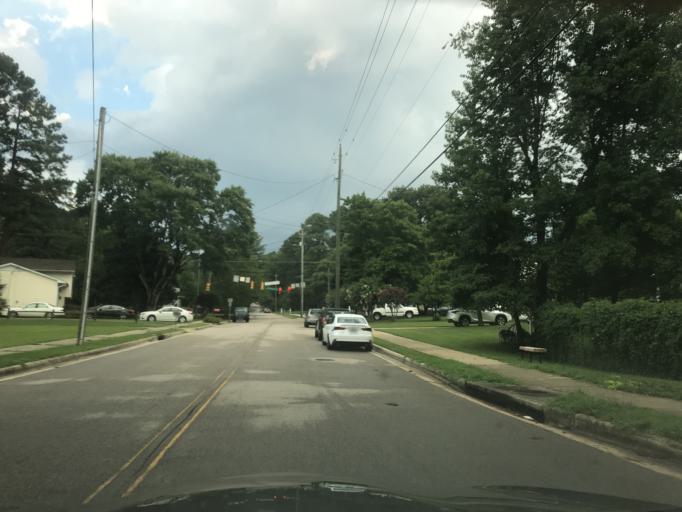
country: US
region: North Carolina
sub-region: Wake County
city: West Raleigh
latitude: 35.8436
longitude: -78.6516
